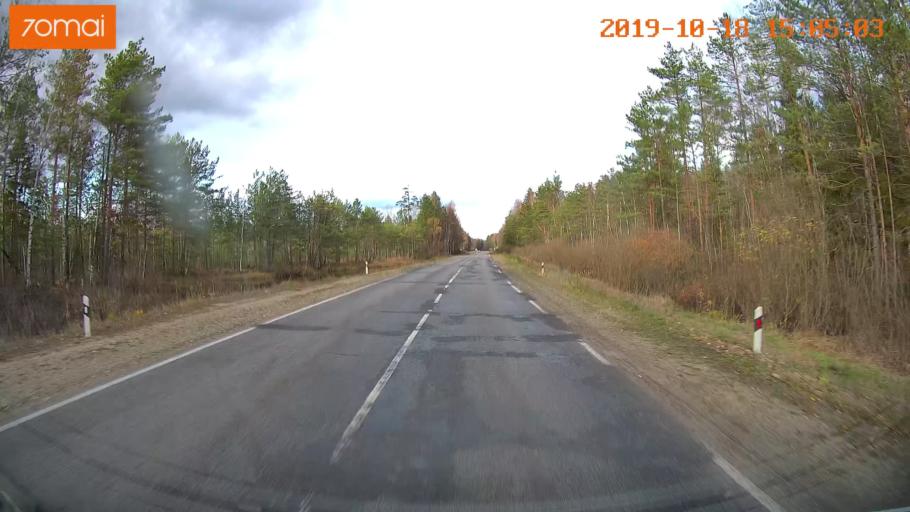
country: RU
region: Vladimir
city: Kurlovo
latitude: 55.5094
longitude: 40.5699
